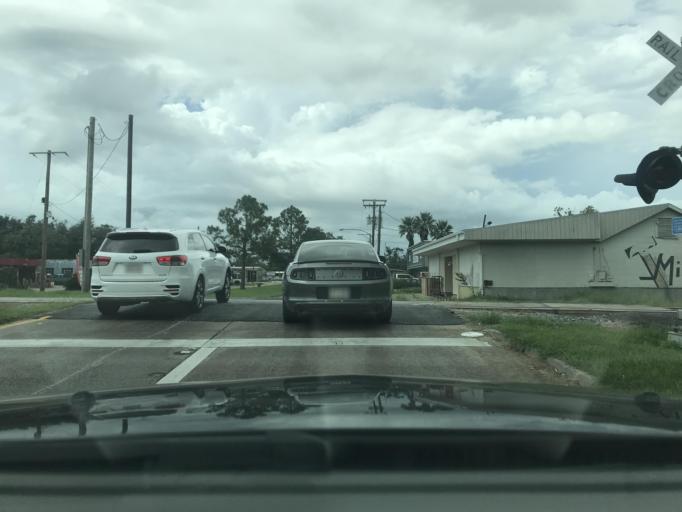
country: US
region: Louisiana
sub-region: Calcasieu Parish
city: Lake Charles
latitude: 30.2130
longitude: -93.2044
